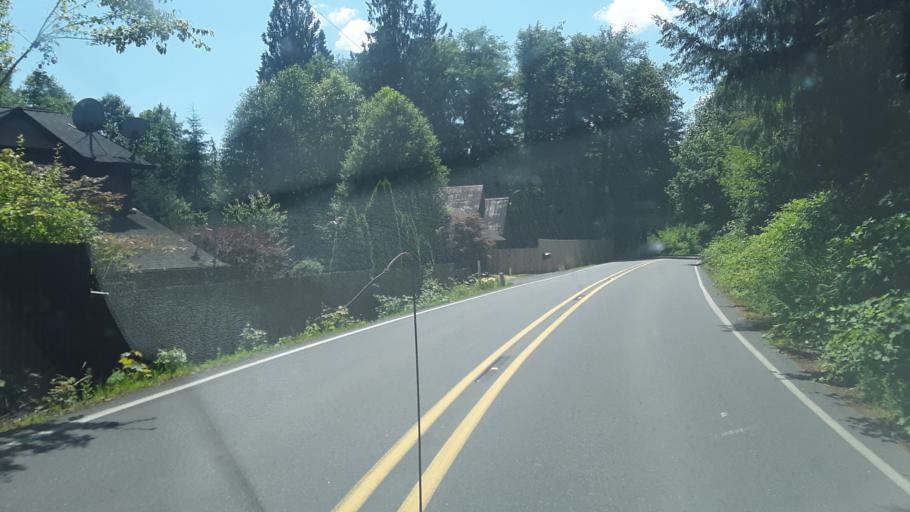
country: US
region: Washington
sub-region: Clark County
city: Amboy
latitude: 45.9072
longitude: -122.4492
